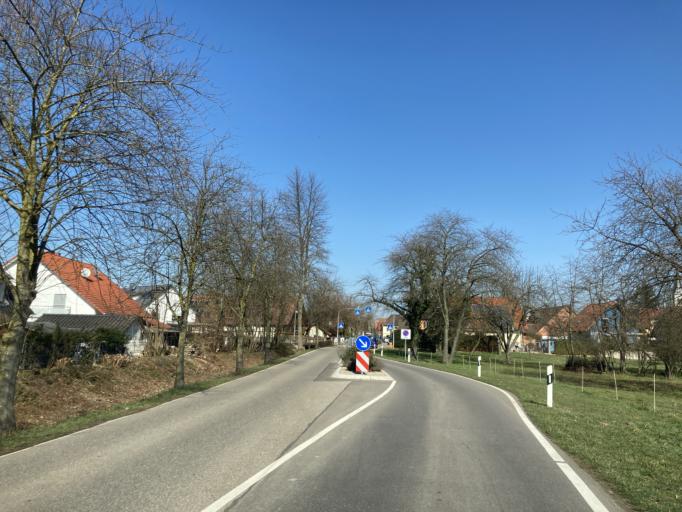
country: DE
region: Baden-Wuerttemberg
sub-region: Freiburg Region
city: Eschbach
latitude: 47.8871
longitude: 7.6501
